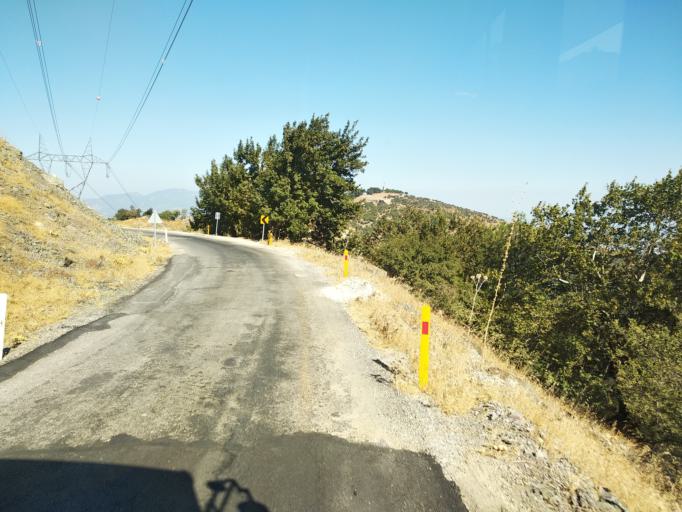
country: TR
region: Izmir
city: Gaziemir
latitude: 38.3152
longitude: 27.0078
